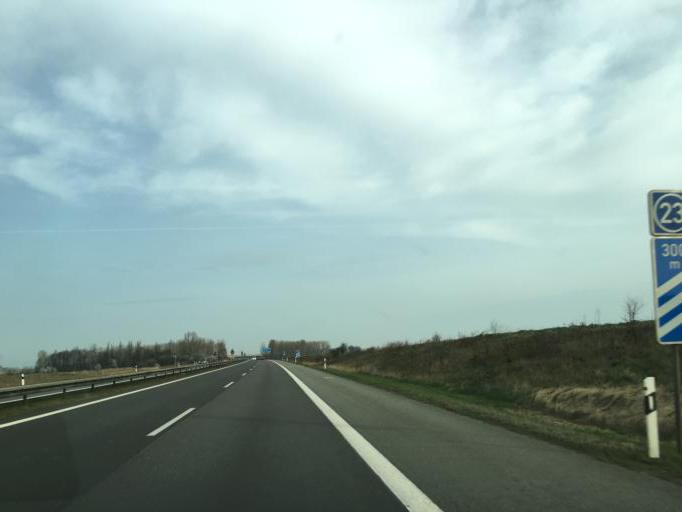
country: DE
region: Brandenburg
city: Fehrbellin
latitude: 52.8423
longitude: 12.7856
